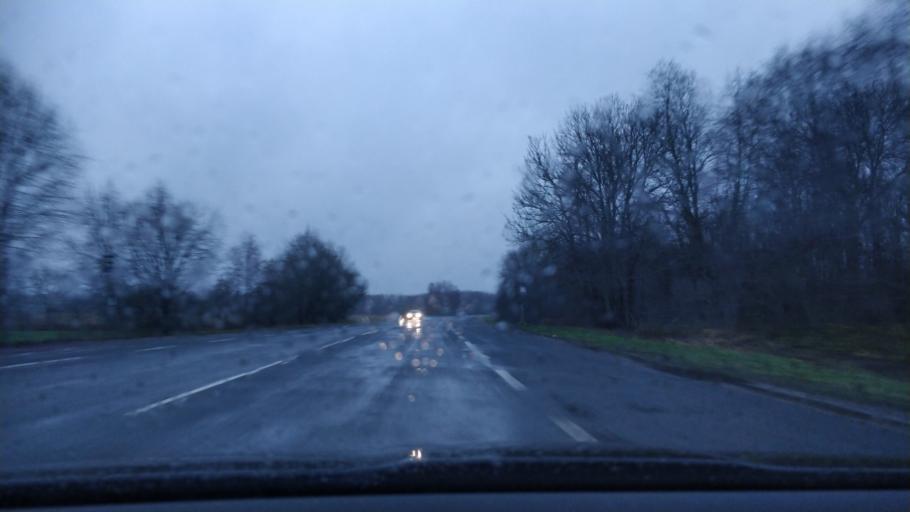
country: EE
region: Laeaene
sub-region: Lihula vald
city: Lihula
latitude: 58.7062
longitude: 23.8625
